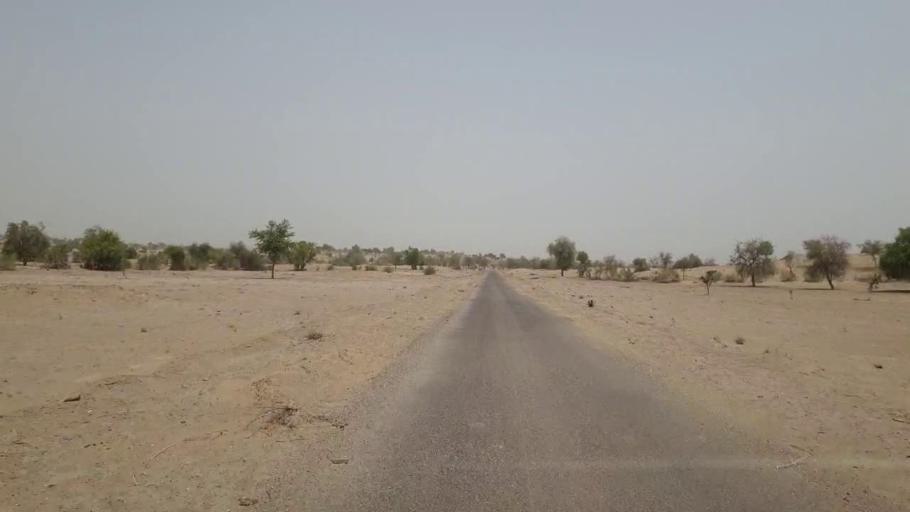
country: PK
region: Sindh
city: Islamkot
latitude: 24.8065
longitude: 70.5370
